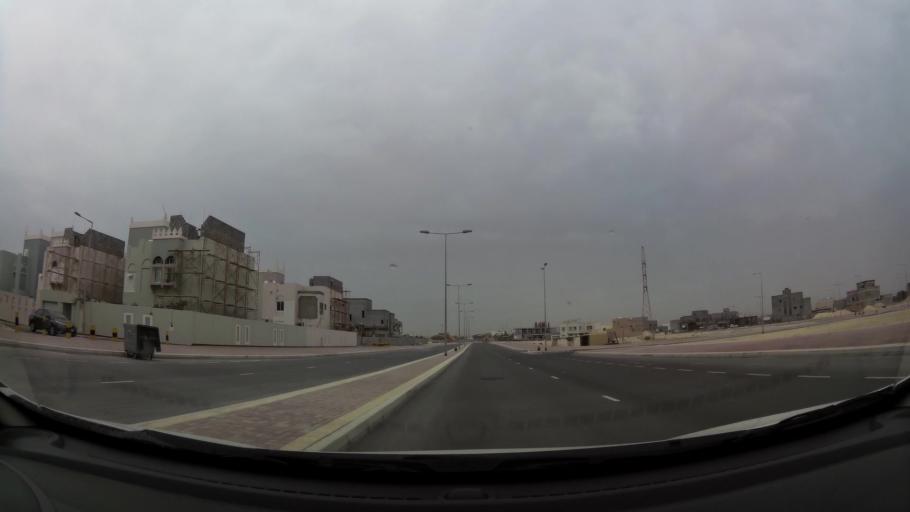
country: BH
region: Northern
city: Madinat `Isa
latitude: 26.1656
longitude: 50.5392
